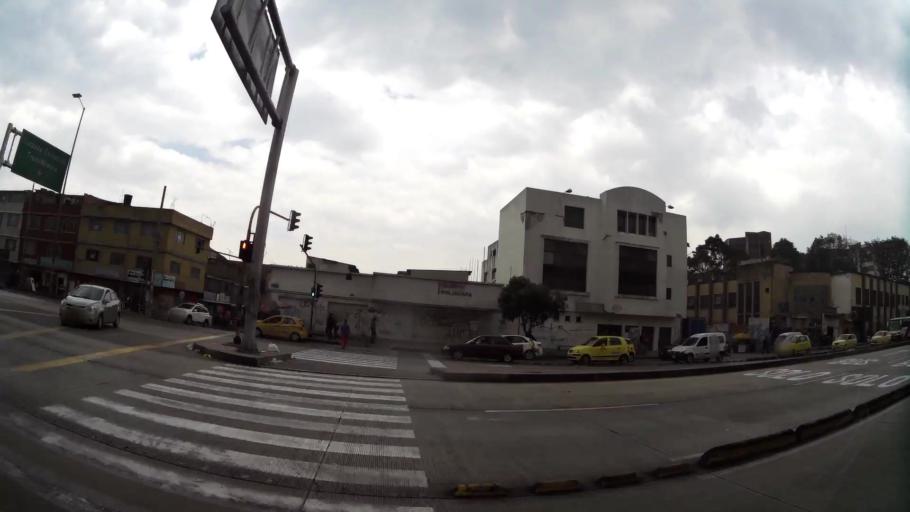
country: CO
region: Bogota D.C.
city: Bogota
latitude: 4.5870
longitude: -74.0863
